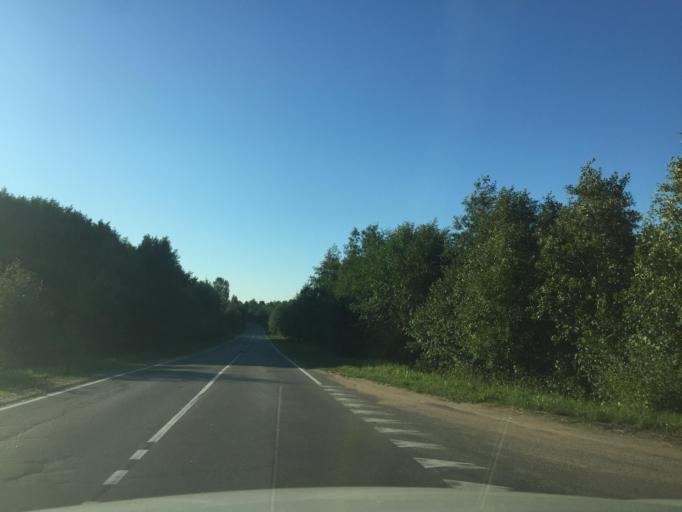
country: RU
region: Leningrad
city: Siverskiy
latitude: 59.3387
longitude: 30.0260
